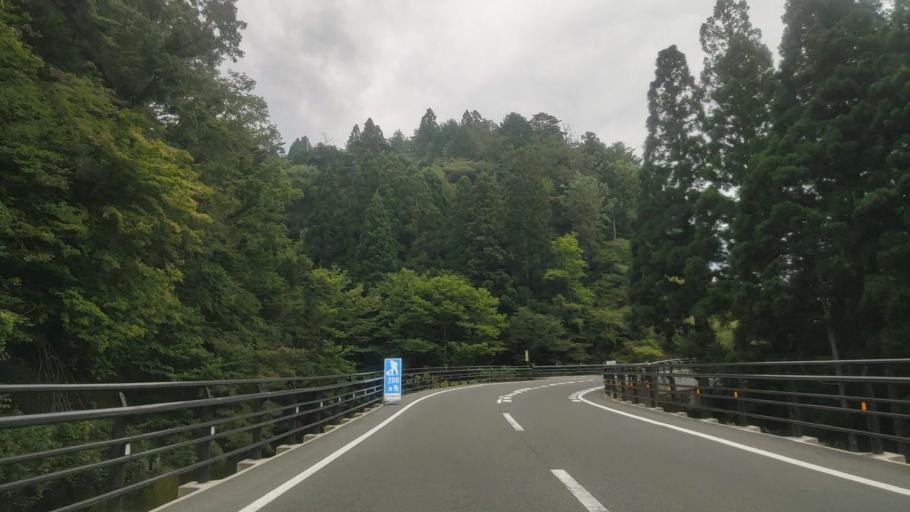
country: JP
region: Wakayama
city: Koya
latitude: 34.2188
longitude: 135.5671
